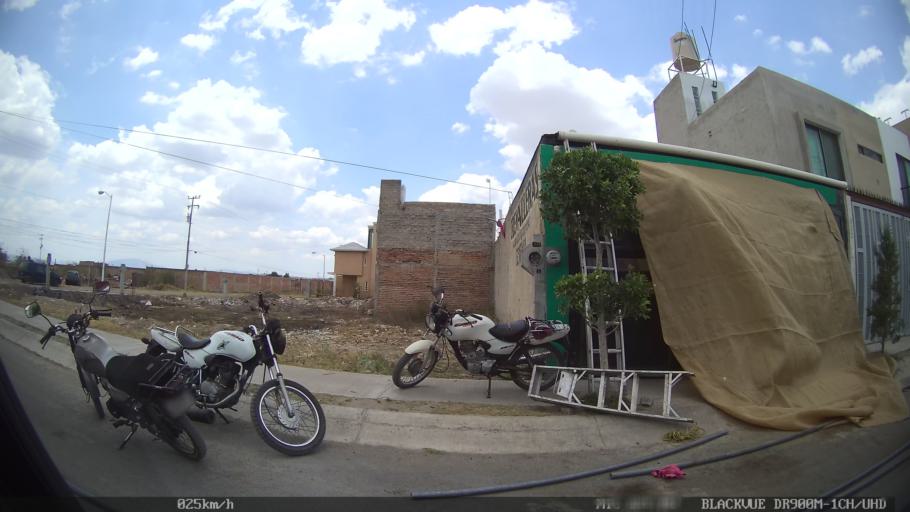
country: MX
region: Jalisco
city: Coyula
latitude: 20.6641
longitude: -103.2210
